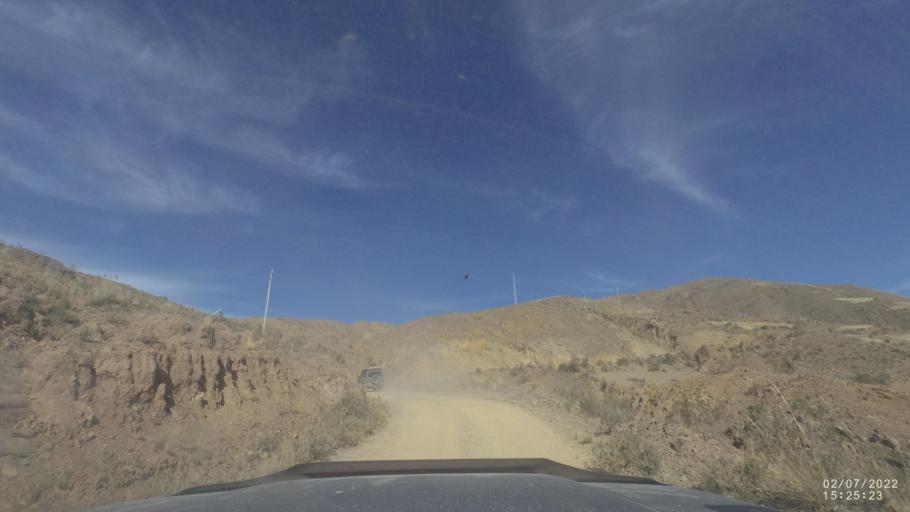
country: BO
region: Cochabamba
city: Irpa Irpa
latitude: -17.8758
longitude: -66.4159
